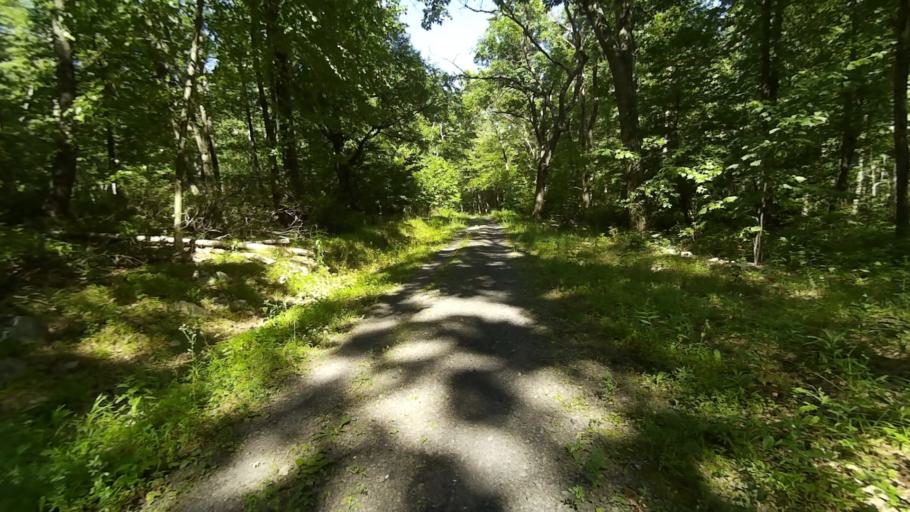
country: US
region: Pennsylvania
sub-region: Centre County
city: Boalsburg
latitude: 40.7358
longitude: -77.7660
